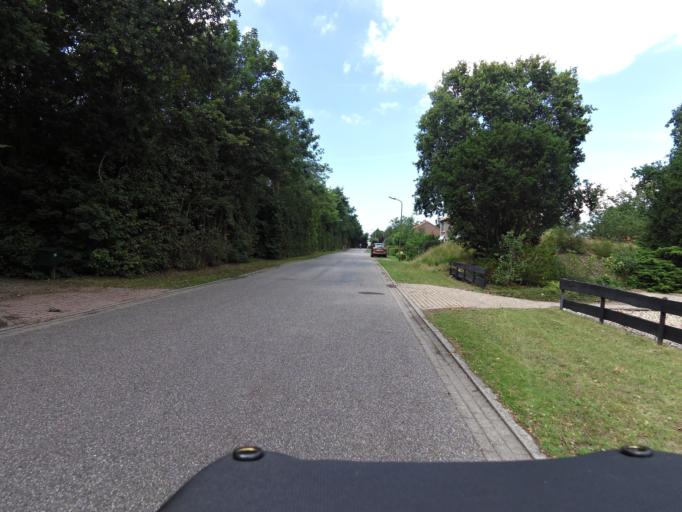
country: NL
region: South Holland
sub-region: Gemeente Goeree-Overflakkee
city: Ouddorp
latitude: 51.8192
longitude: 3.9316
